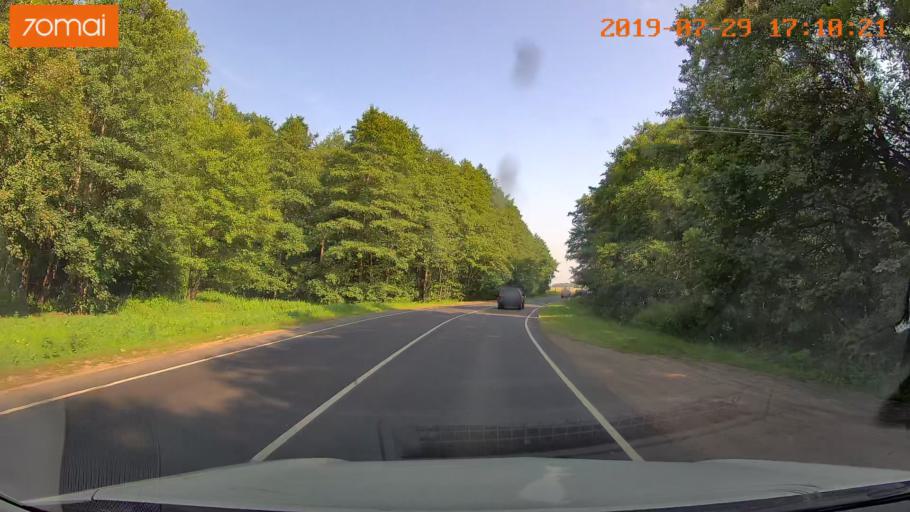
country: RU
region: Kaliningrad
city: Vzmorye
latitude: 54.8028
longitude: 20.3675
